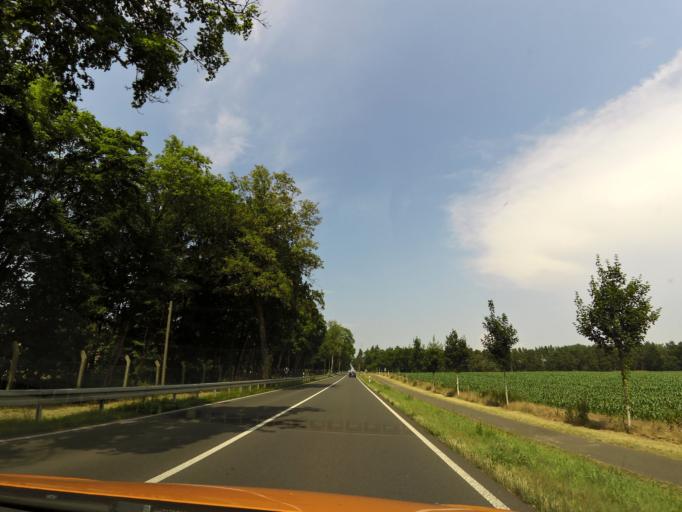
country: DE
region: Brandenburg
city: Pritzwalk
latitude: 53.1737
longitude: 12.1882
